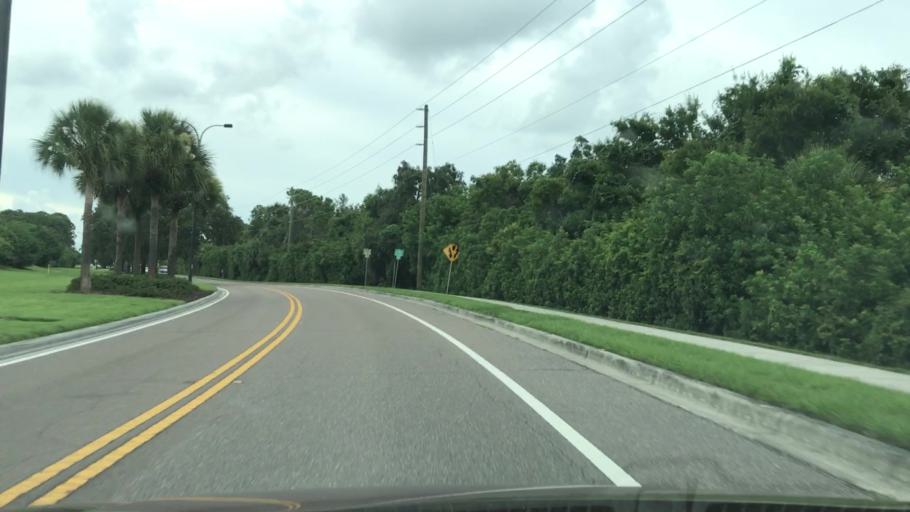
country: US
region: Florida
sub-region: Sarasota County
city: Vamo
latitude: 27.2404
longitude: -82.4737
